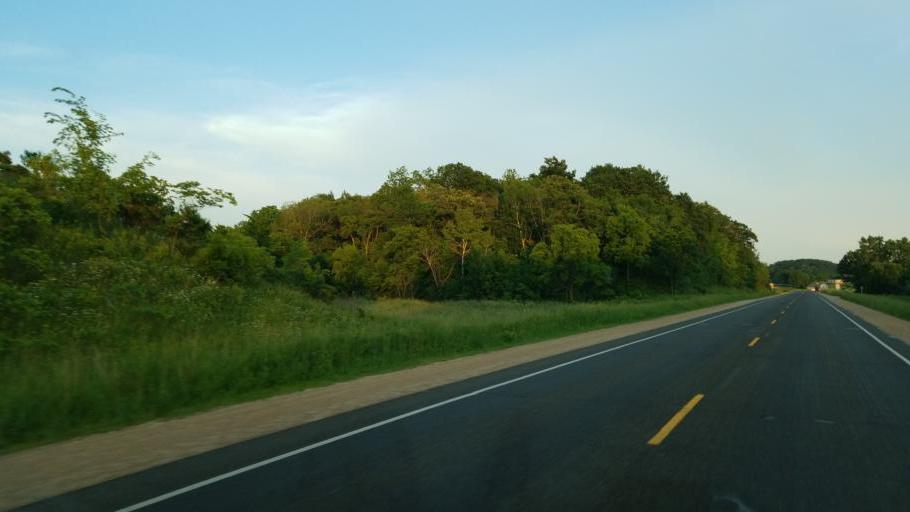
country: US
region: Wisconsin
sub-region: Monroe County
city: Tomah
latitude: 43.9237
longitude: -90.4993
